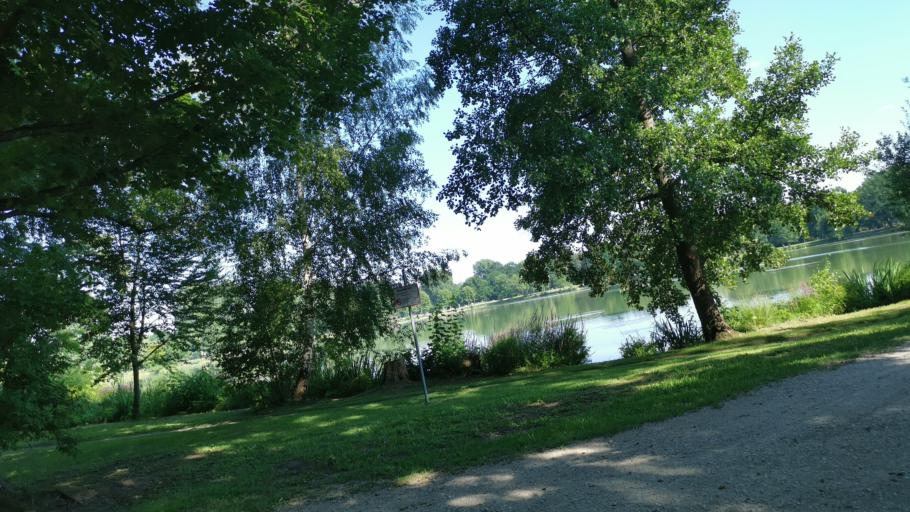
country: DE
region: Bavaria
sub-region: Regierungsbezirk Mittelfranken
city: Nuernberg
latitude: 49.4274
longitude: 11.1080
